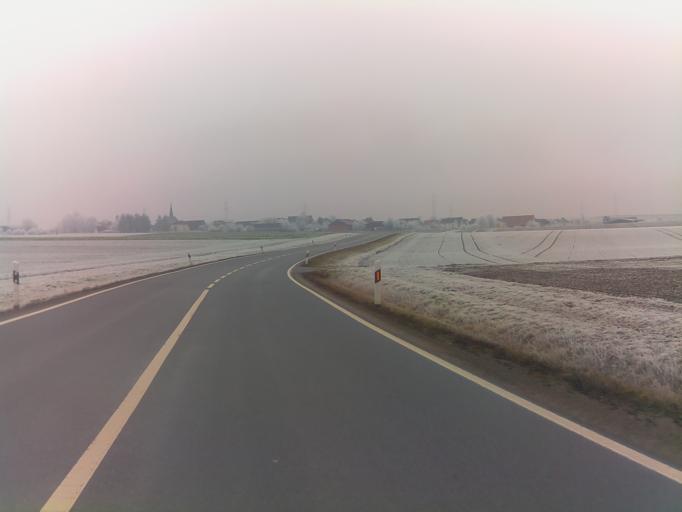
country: DE
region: Bavaria
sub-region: Regierungsbezirk Unterfranken
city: Giebelstadt
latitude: 49.6172
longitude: 9.9615
